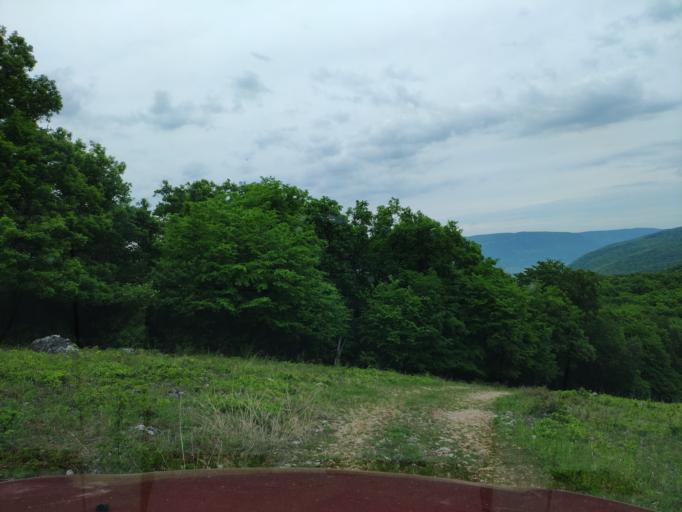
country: SK
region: Kosicky
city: Roznava
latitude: 48.5496
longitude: 20.6172
